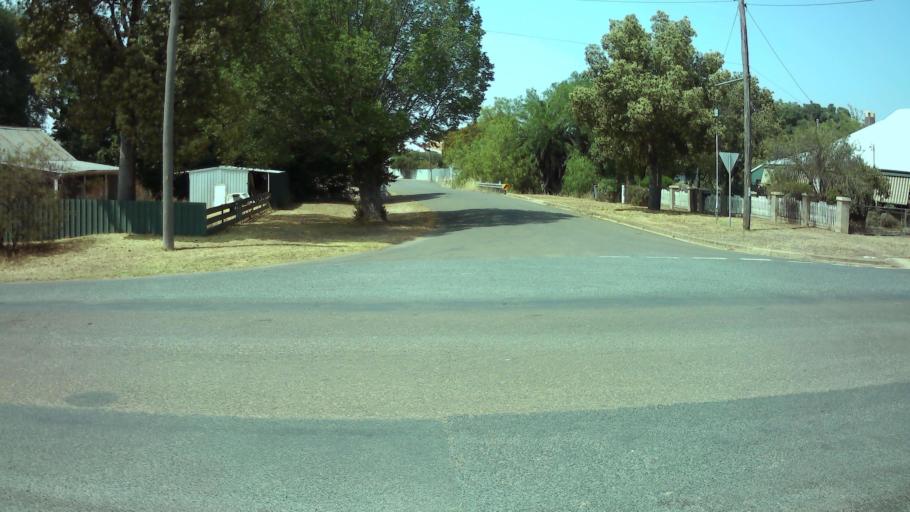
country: AU
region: New South Wales
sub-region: Weddin
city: Grenfell
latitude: -33.8921
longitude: 148.1586
